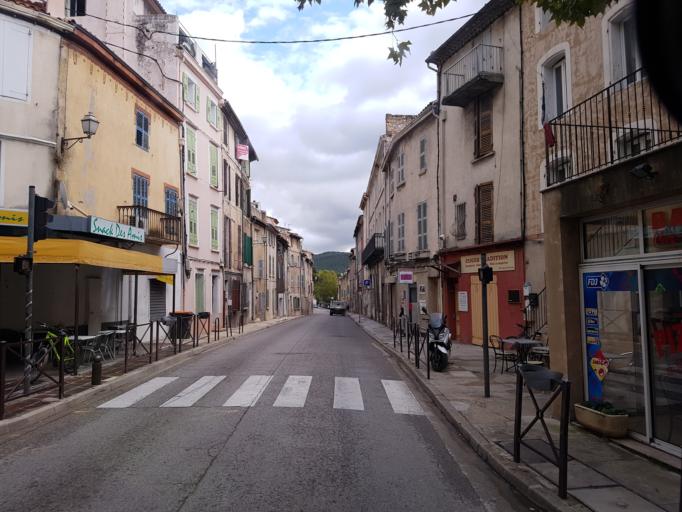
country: FR
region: Provence-Alpes-Cote d'Azur
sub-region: Departement des Bouches-du-Rhone
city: Cuges-les-Pins
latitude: 43.2759
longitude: 5.7019
